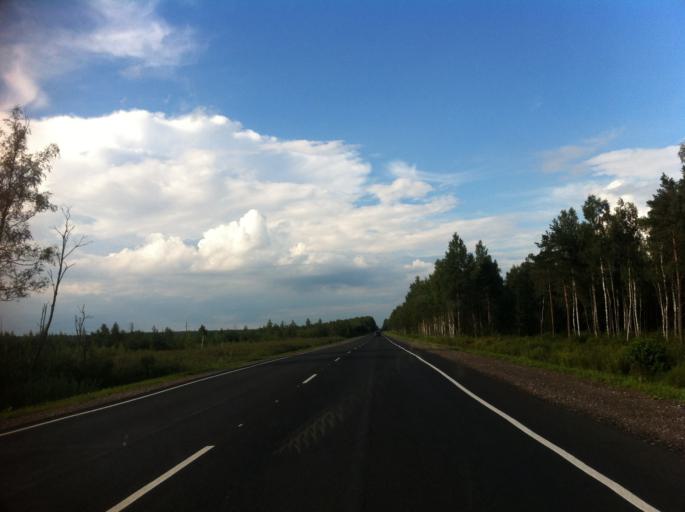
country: RU
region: Leningrad
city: Luga
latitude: 58.4492
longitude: 29.7569
